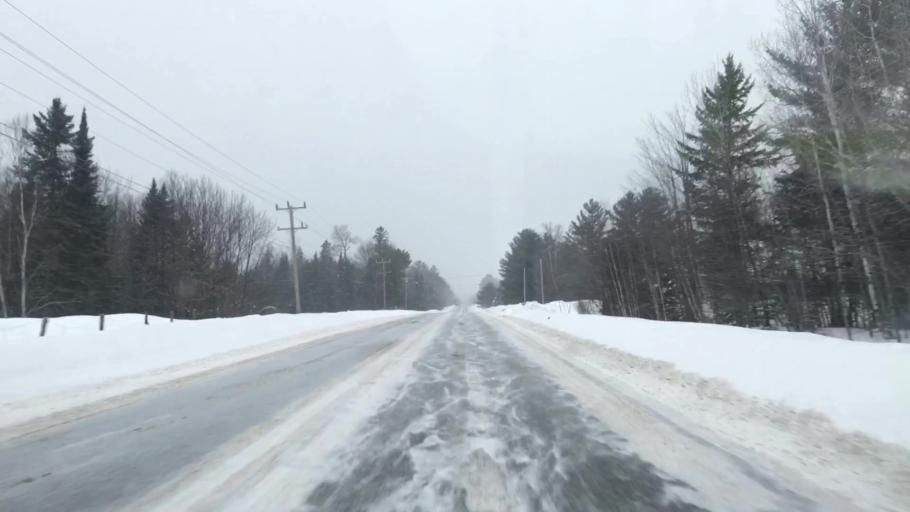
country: US
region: Maine
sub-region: Penobscot County
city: Medway
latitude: 45.5447
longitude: -68.3720
